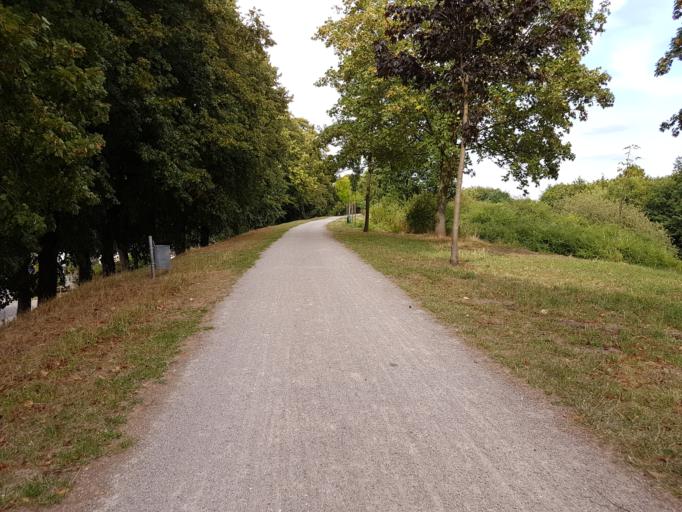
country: DE
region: North Rhine-Westphalia
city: Olfen
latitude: 51.7088
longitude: 7.3860
